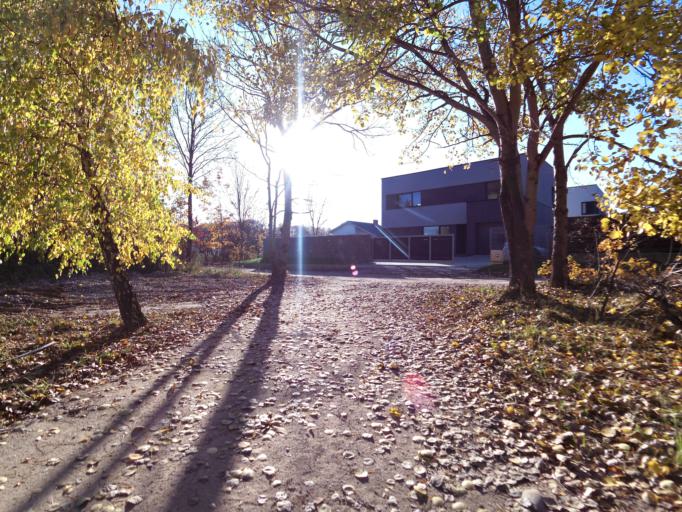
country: LT
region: Vilnius County
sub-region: Vilnius
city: Fabijoniskes
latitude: 54.7450
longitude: 25.2613
